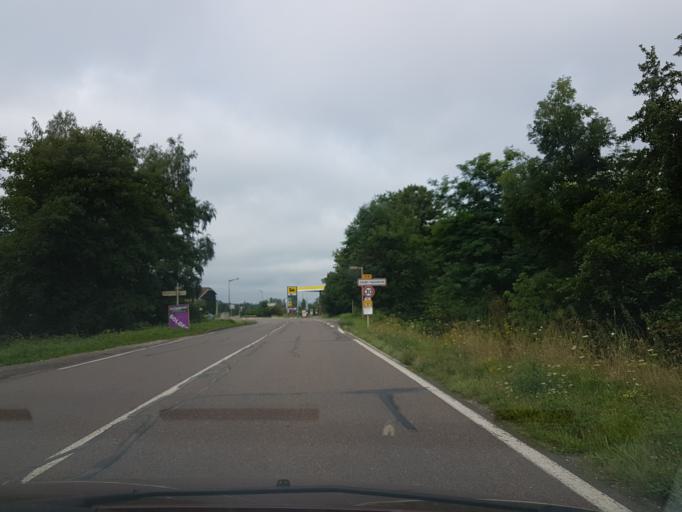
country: FR
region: Franche-Comte
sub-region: Departement de la Haute-Saone
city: Saint-Sauveur
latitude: 47.8096
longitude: 6.3850
